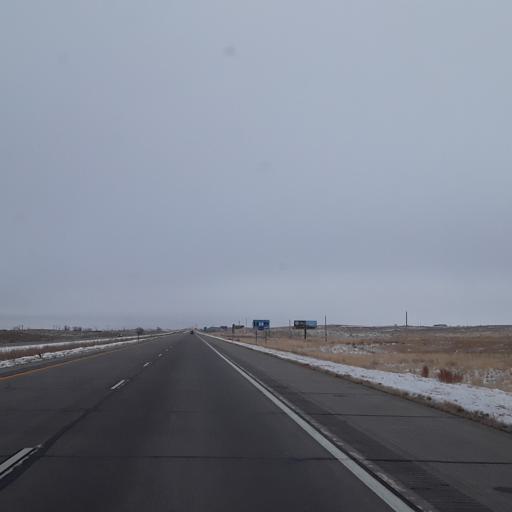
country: US
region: Colorado
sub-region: Logan County
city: Sterling
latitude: 40.5967
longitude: -103.1871
